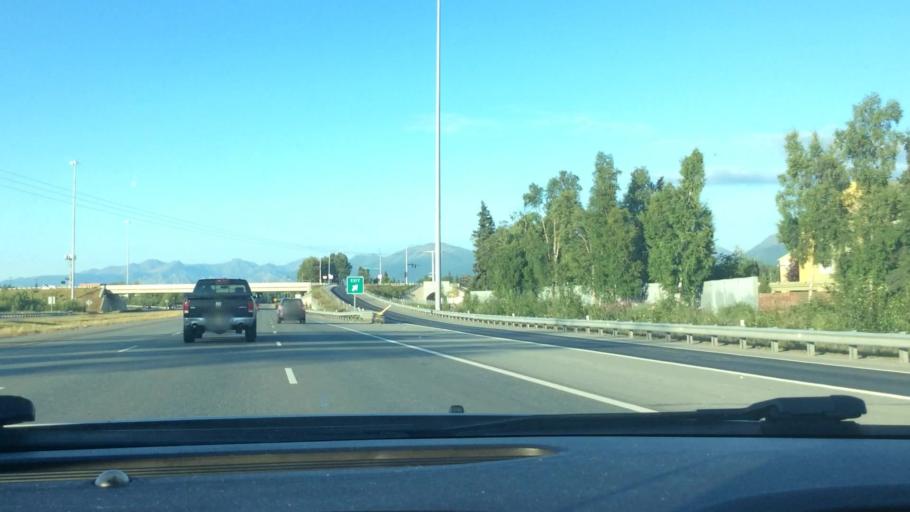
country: US
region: Alaska
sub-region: Anchorage Municipality
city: Anchorage
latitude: 61.2198
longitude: -149.8133
